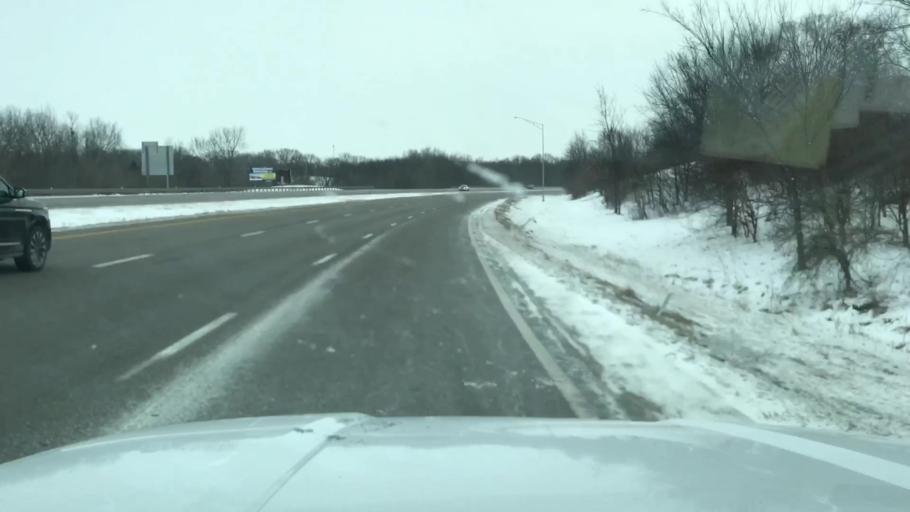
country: US
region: Missouri
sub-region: Andrew County
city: Country Club Village
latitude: 39.8556
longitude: -94.8074
